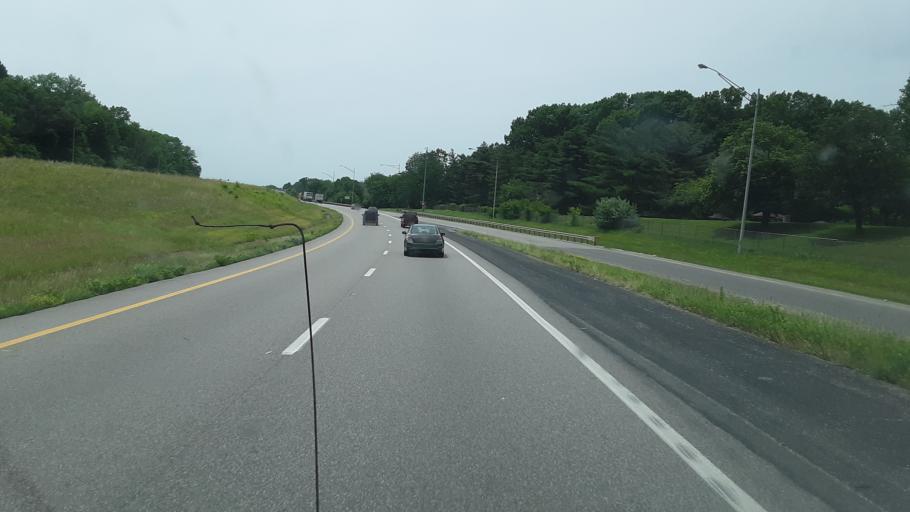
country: US
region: Missouri
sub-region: Saint Louis County
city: Glasgow Village
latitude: 38.7677
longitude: -90.1847
